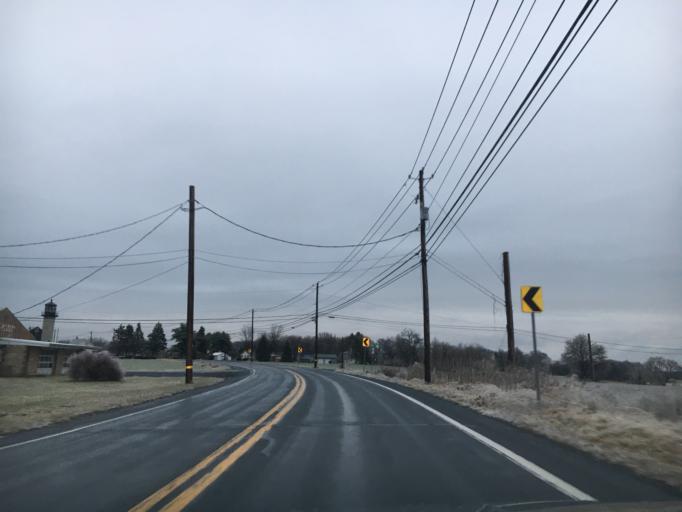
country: US
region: Pennsylvania
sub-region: Lehigh County
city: Schnecksville
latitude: 40.6138
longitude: -75.6480
